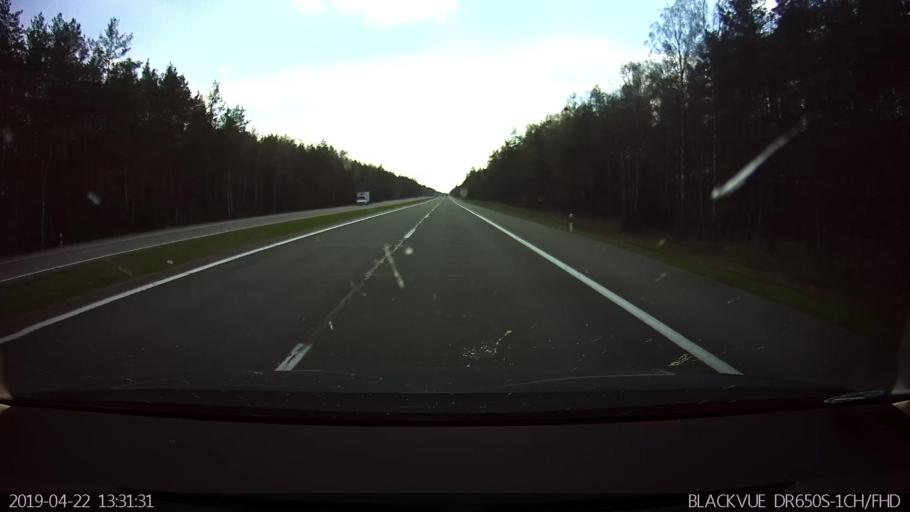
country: BY
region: Grodnenskaya
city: Zhyrovichy
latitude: 52.8884
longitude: 25.6676
